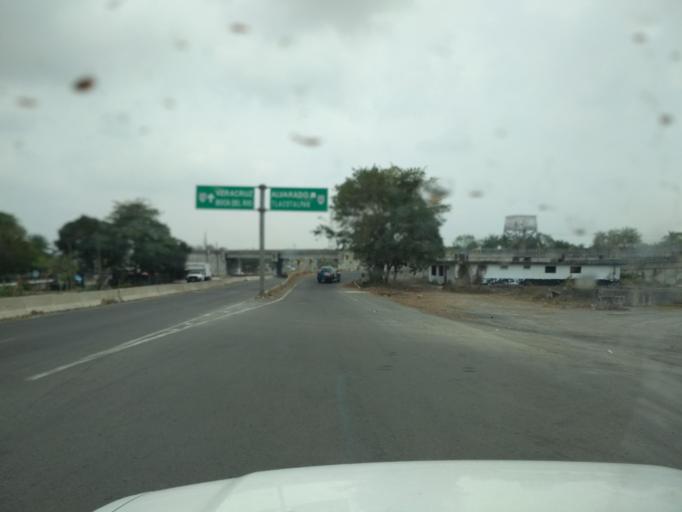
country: MX
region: Veracruz
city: Paso del Toro
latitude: 19.0220
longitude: -96.1351
